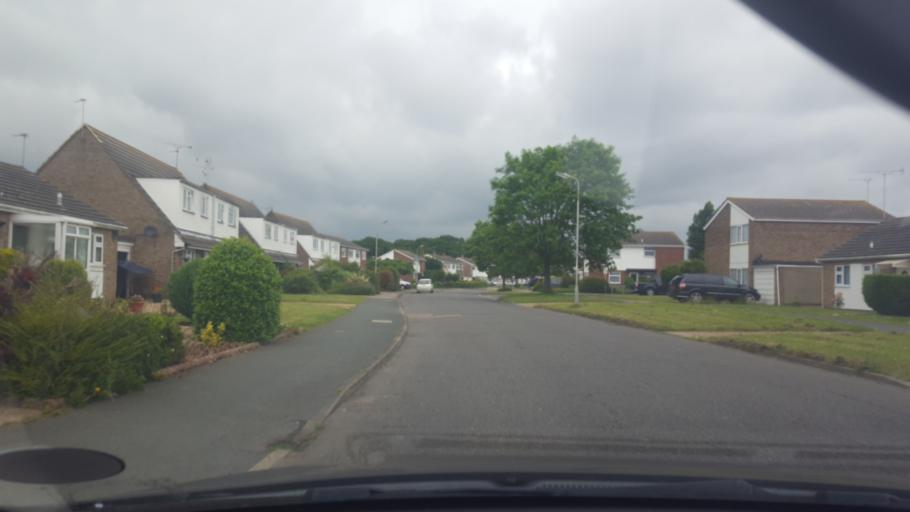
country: GB
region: England
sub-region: Essex
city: Little Clacton
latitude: 51.7995
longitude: 1.1246
